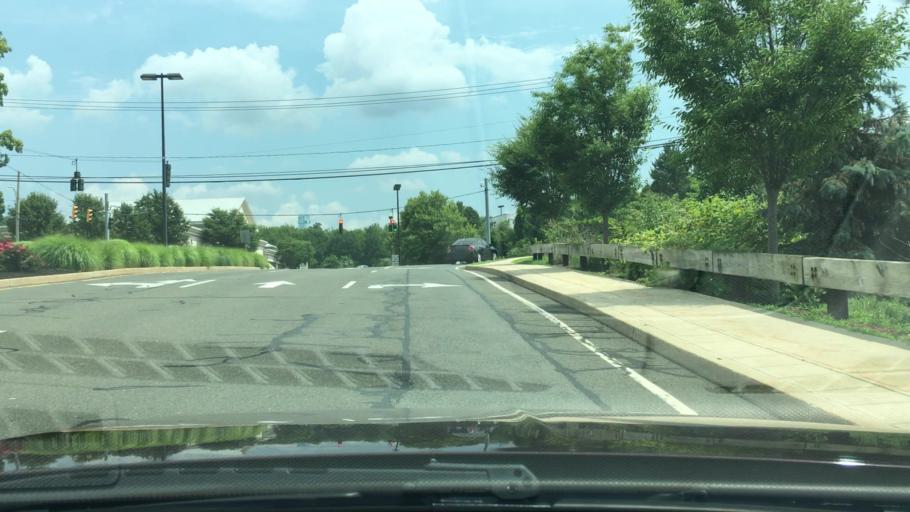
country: US
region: Connecticut
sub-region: Hartford County
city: Manchester
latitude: 41.8104
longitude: -72.5558
